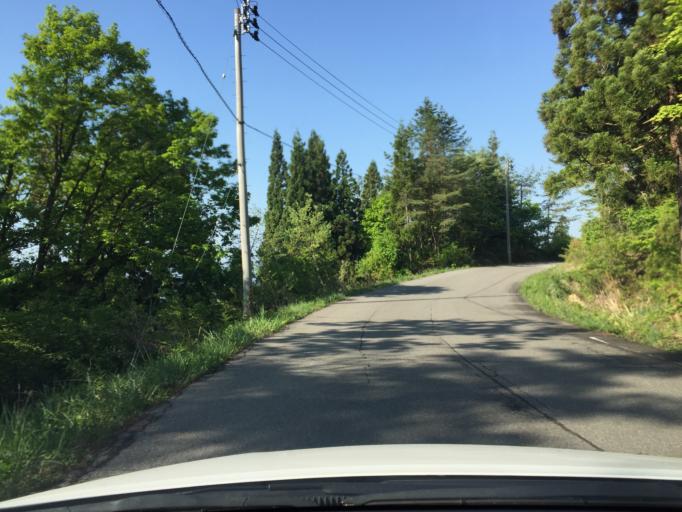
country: JP
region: Fukushima
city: Kitakata
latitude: 37.6834
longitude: 139.6918
